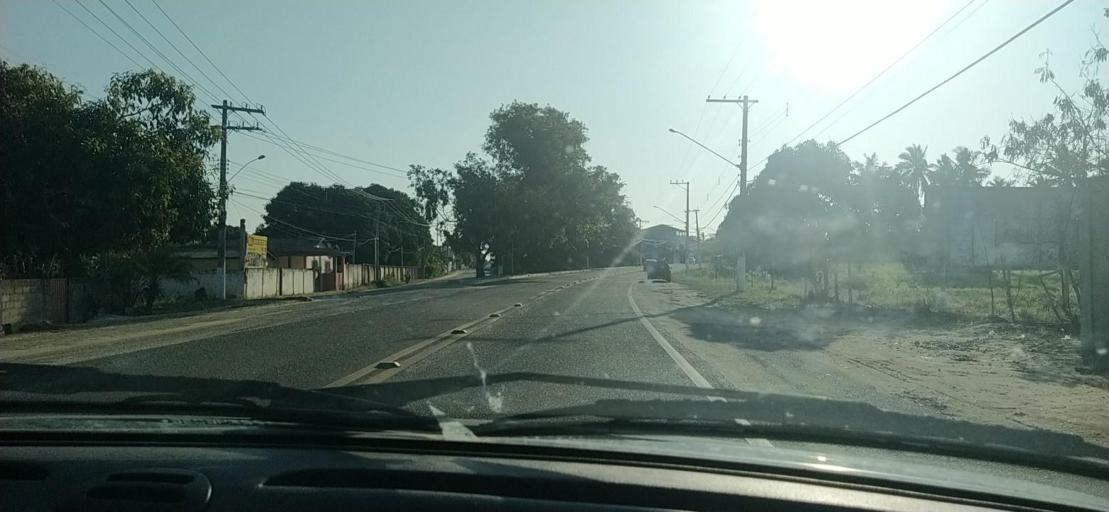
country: BR
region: Espirito Santo
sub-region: Conceicao Da Barra
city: Conceicao da Barra
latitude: -18.5681
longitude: -39.7495
